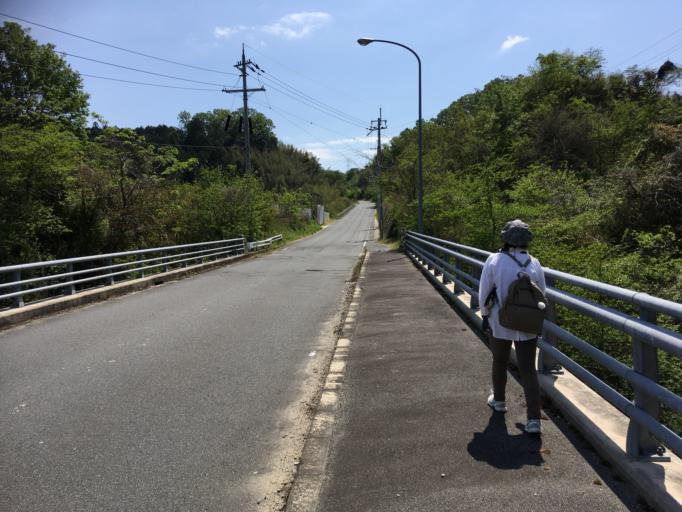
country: JP
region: Nara
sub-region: Ikoma-shi
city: Ikoma
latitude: 34.6410
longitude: 135.6786
